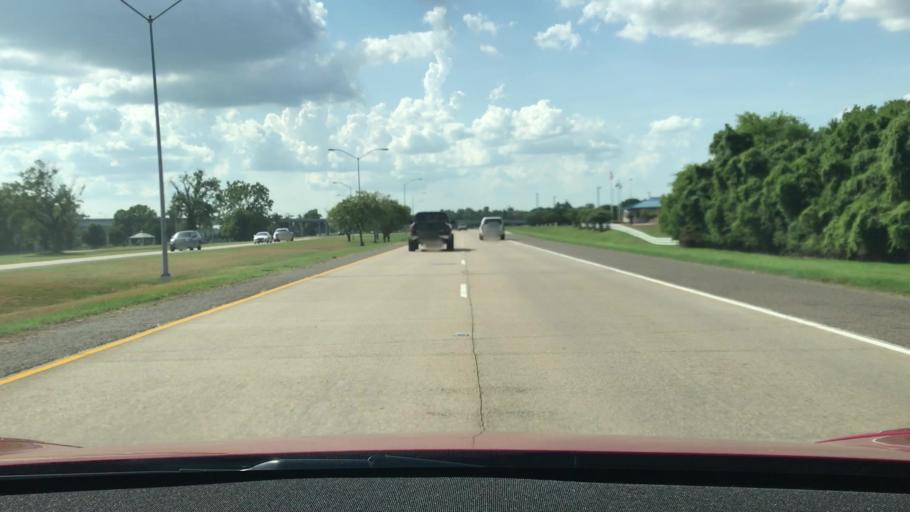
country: US
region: Louisiana
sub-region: Bossier Parish
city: Bossier City
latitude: 32.4900
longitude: -93.6915
